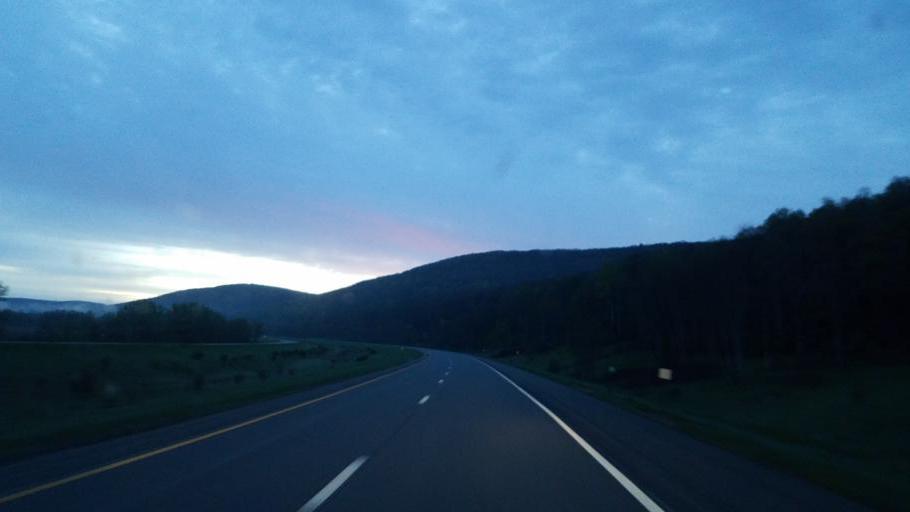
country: US
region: New York
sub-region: Allegany County
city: Cuba
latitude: 42.1814
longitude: -78.3536
